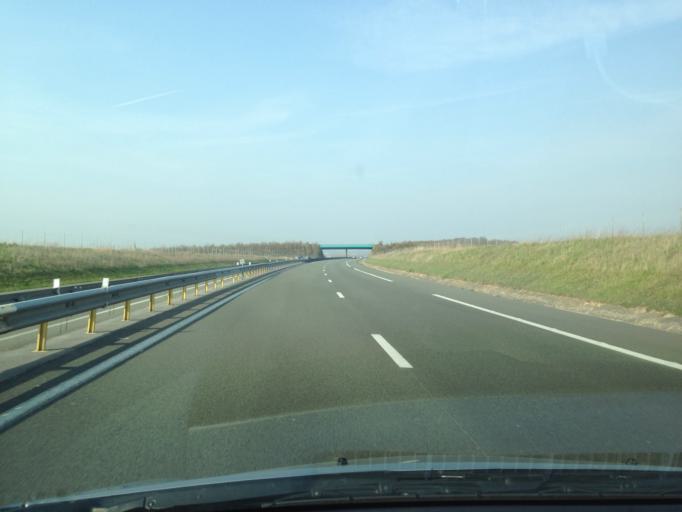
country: FR
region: Picardie
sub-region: Departement de la Somme
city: Sailly-Flibeaucourt
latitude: 50.1817
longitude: 1.7531
